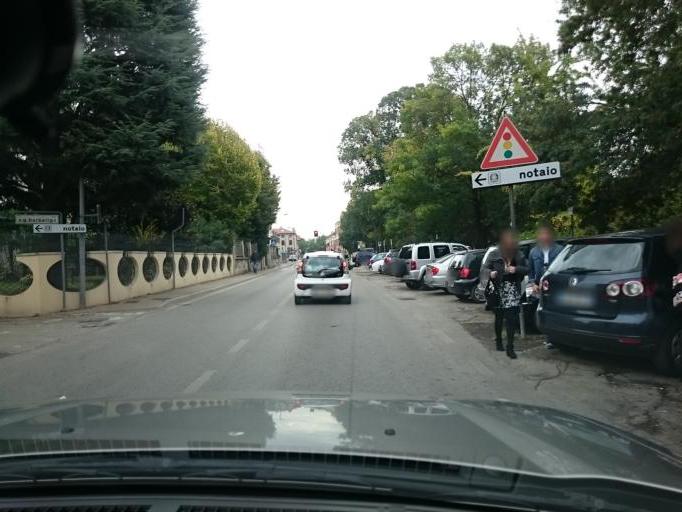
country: IT
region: Veneto
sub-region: Provincia di Padova
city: Piove di Sacco-Piovega
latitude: 45.2988
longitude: 12.0338
